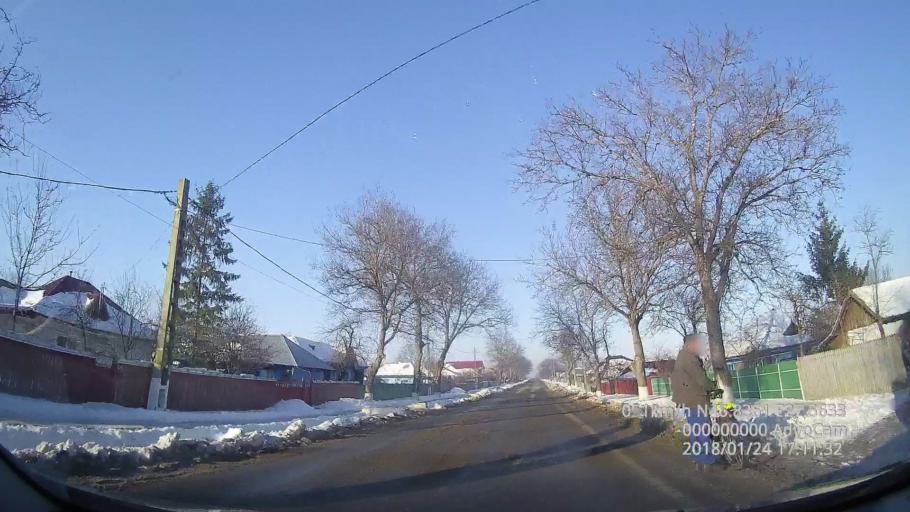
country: RO
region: Vaslui
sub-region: Comuna Rebricea
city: Rebricea
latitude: 46.8364
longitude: 27.5633
